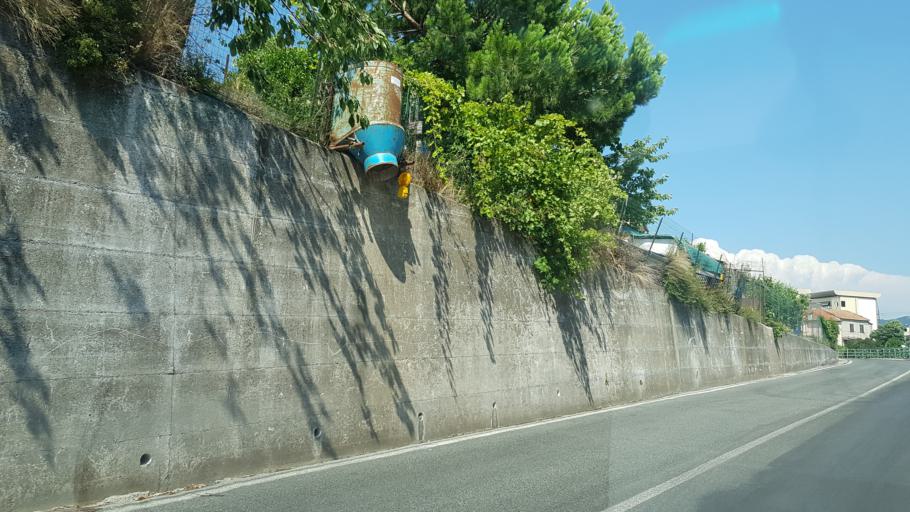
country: IT
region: Liguria
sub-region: Provincia di Genova
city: San Teodoro
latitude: 44.4355
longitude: 8.8683
